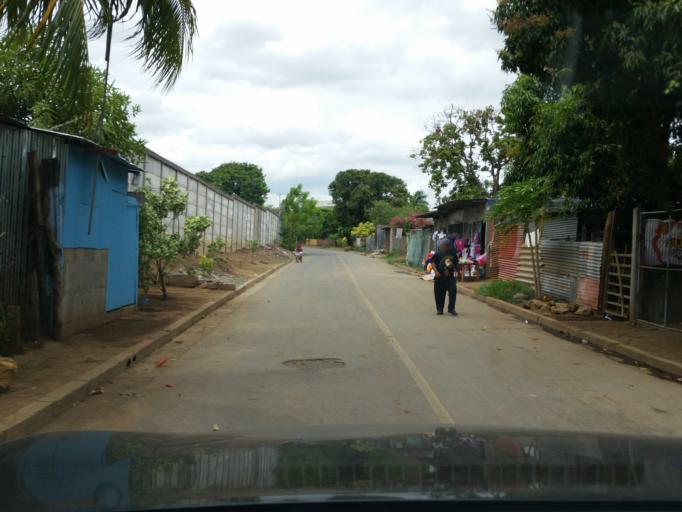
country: NI
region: Managua
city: Managua
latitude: 12.1322
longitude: -86.2617
